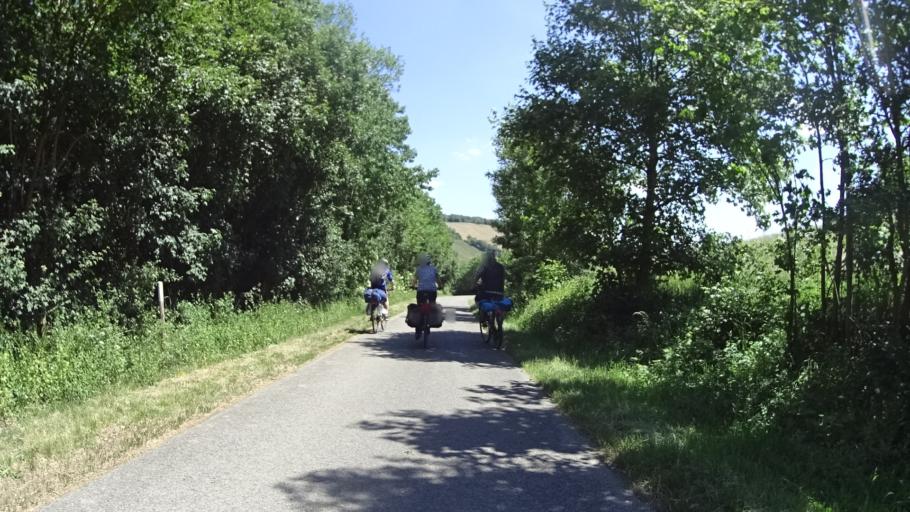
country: DE
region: Bavaria
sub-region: Regierungsbezirk Mittelfranken
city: Adelshofen
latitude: 49.4457
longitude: 10.1167
